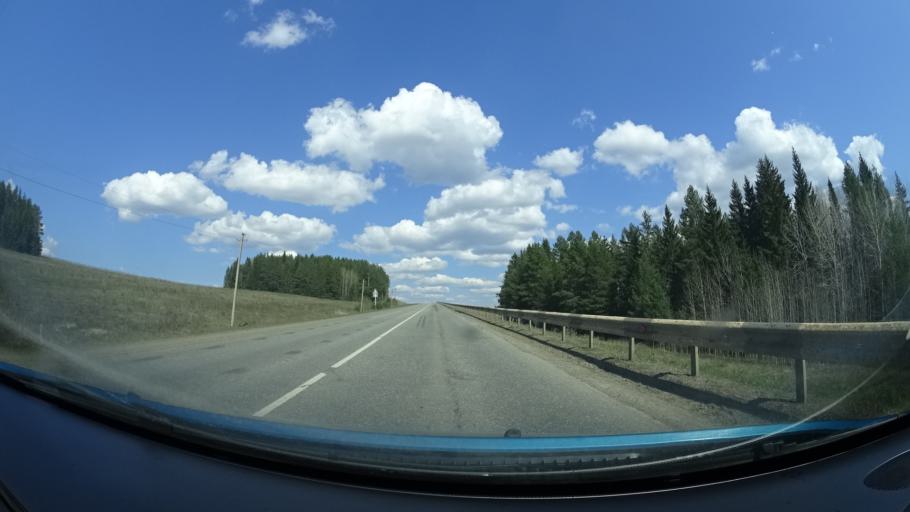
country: RU
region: Perm
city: Osa
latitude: 57.3120
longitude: 55.6211
